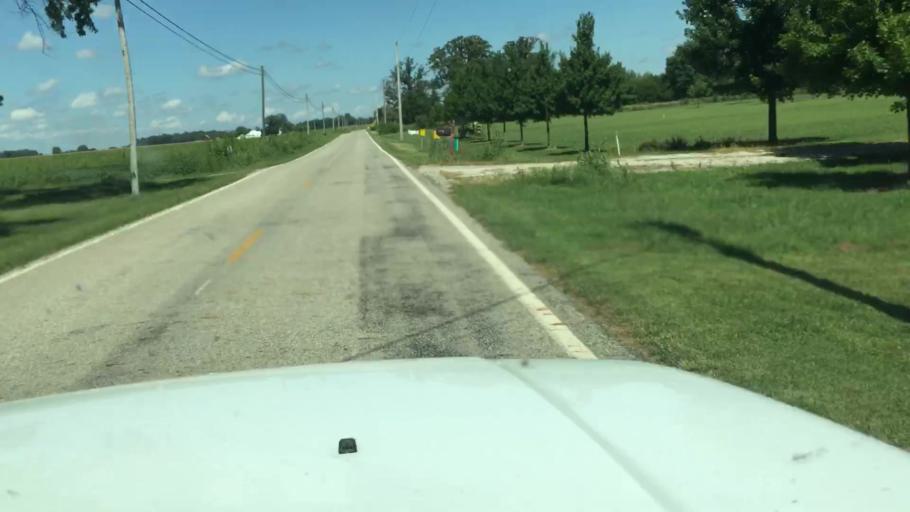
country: US
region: Ohio
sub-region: Madison County
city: Mount Sterling
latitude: 39.6721
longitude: -83.2352
